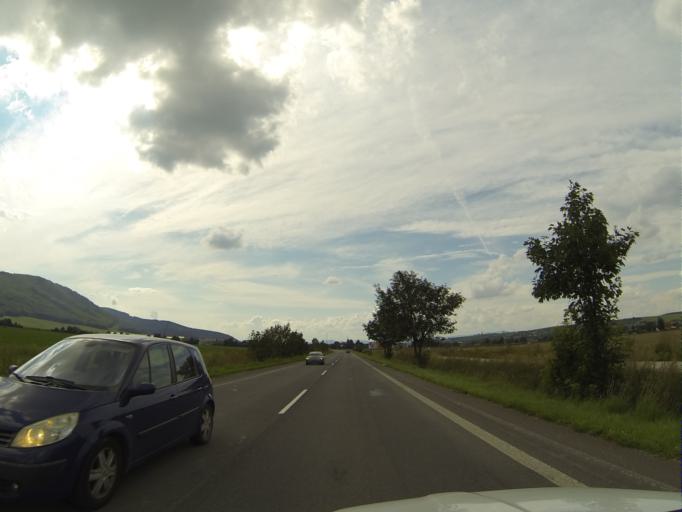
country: SK
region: Nitriansky
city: Partizanske
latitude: 48.6258
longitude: 18.4383
